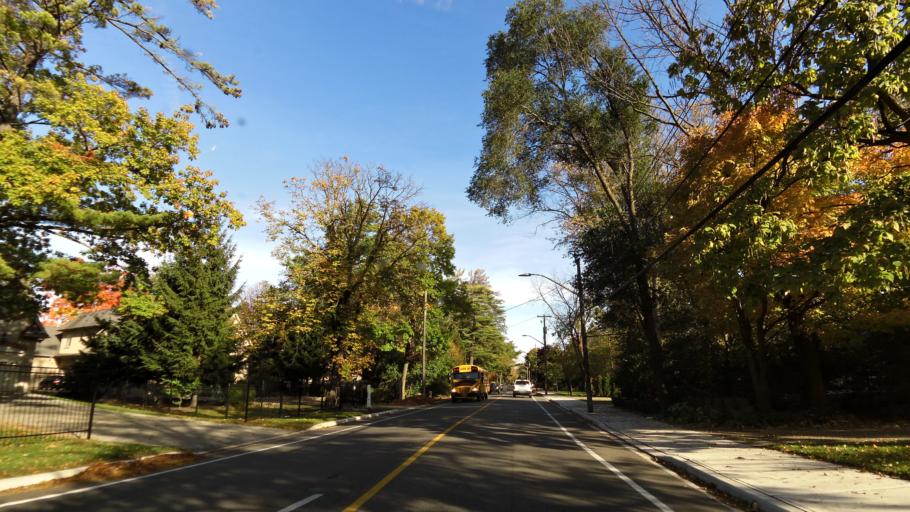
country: CA
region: Ontario
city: Mississauga
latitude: 43.5510
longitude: -79.6013
